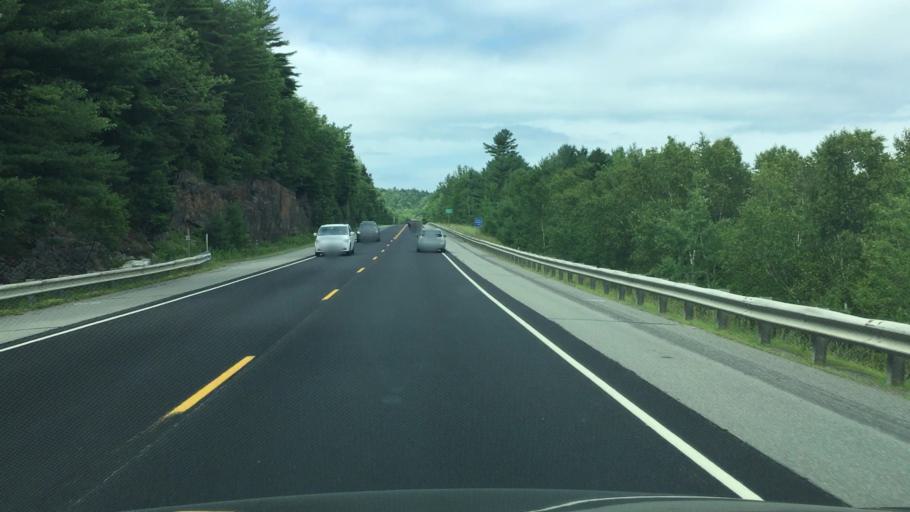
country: US
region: Maine
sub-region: Hancock County
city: Bucksport
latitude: 44.5480
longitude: -68.8092
